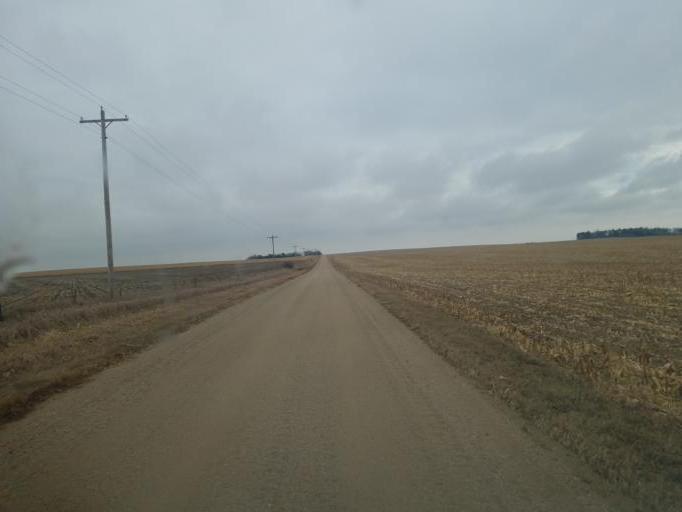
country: US
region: Nebraska
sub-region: Pierce County
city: Plainview
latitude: 42.3798
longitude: -97.7909
